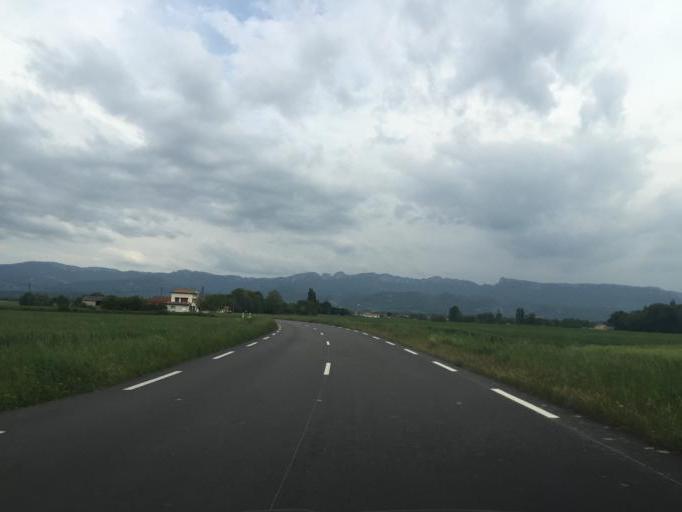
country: FR
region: Rhone-Alpes
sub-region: Departement de la Drome
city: Alixan
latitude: 44.9724
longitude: 5.0465
